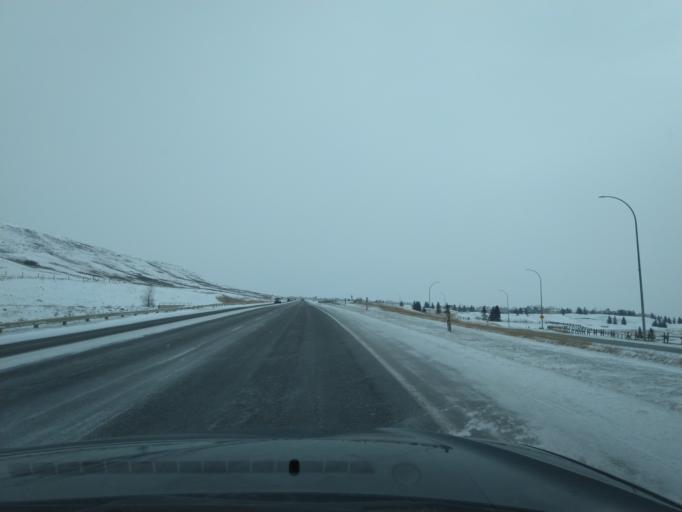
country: CA
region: Alberta
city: Cochrane
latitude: 51.1911
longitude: -114.4531
